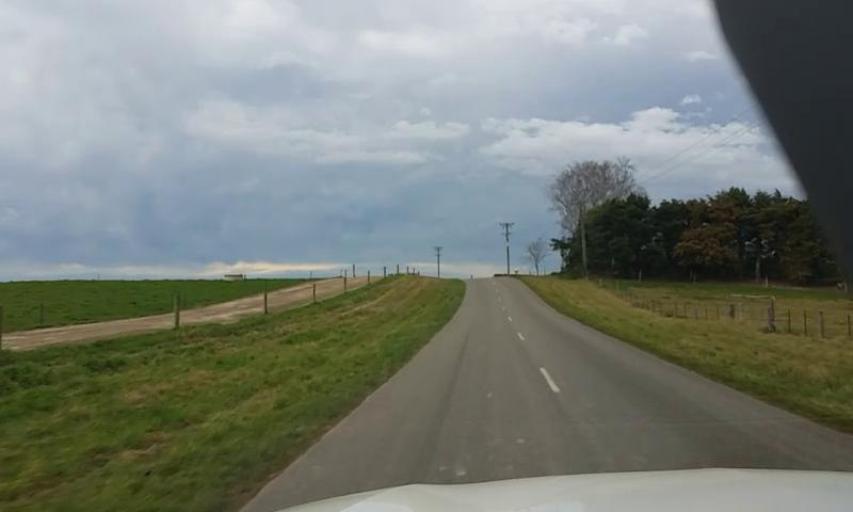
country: NZ
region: Canterbury
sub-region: Waimakariri District
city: Kaiapoi
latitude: -43.2960
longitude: 172.4758
